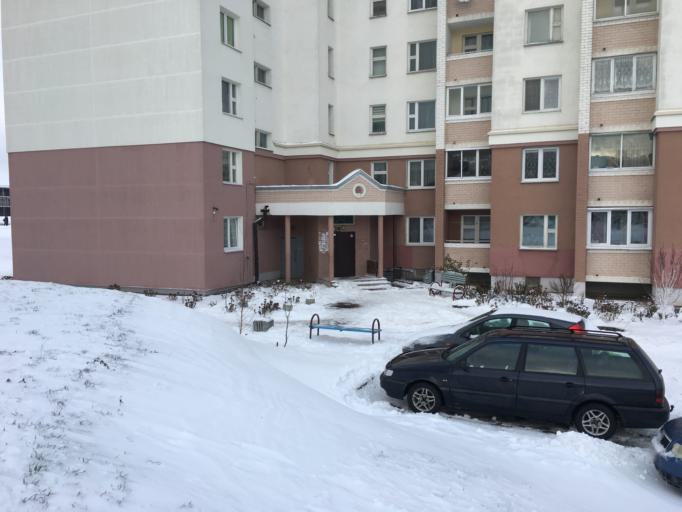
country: BY
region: Grodnenskaya
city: Hrodna
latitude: 53.7153
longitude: 23.8415
